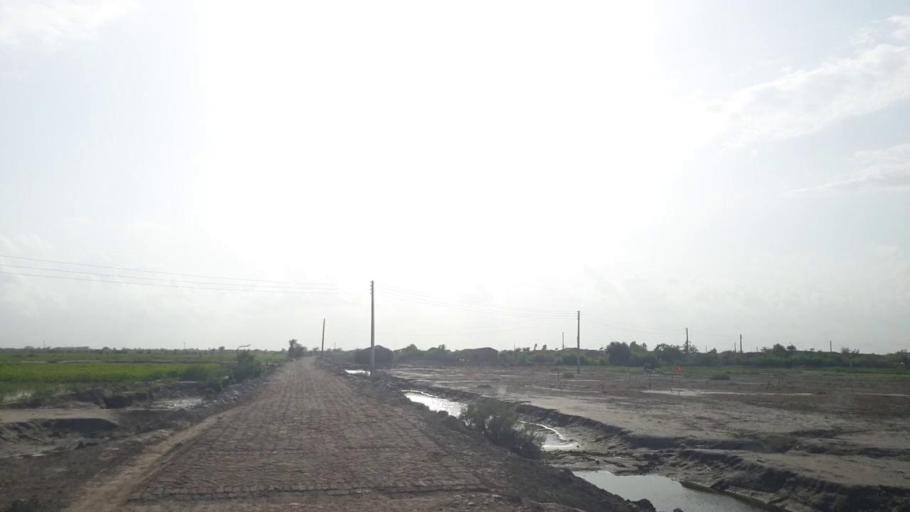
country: PK
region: Sindh
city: Kadhan
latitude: 24.6047
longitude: 69.0871
